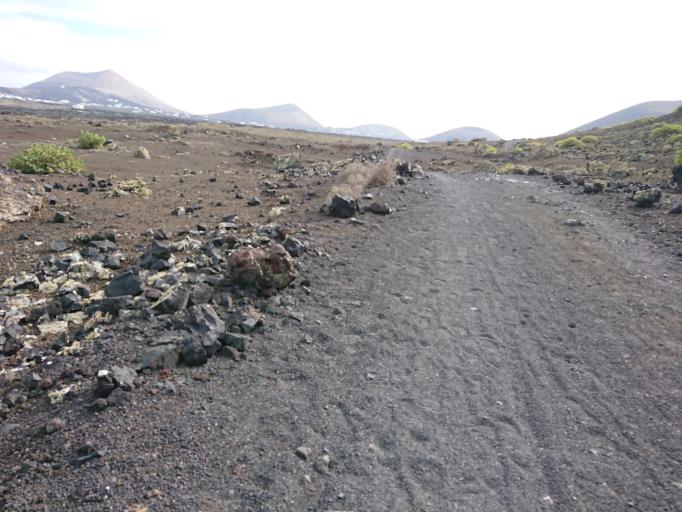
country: ES
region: Canary Islands
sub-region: Provincia de Las Palmas
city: Tinajo
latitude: 29.0076
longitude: -13.6757
